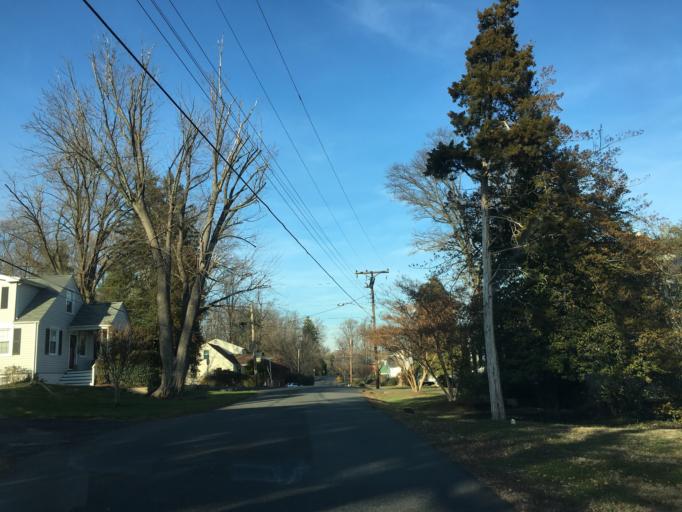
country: US
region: Virginia
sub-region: City of Fairfax
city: Fairfax
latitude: 38.8576
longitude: -77.3141
